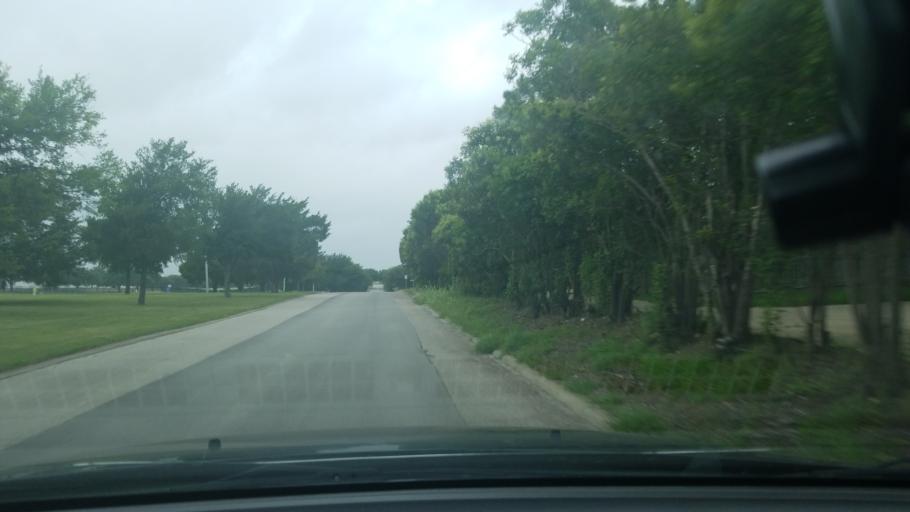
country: US
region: Texas
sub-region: Dallas County
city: Mesquite
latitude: 32.7803
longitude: -96.6380
